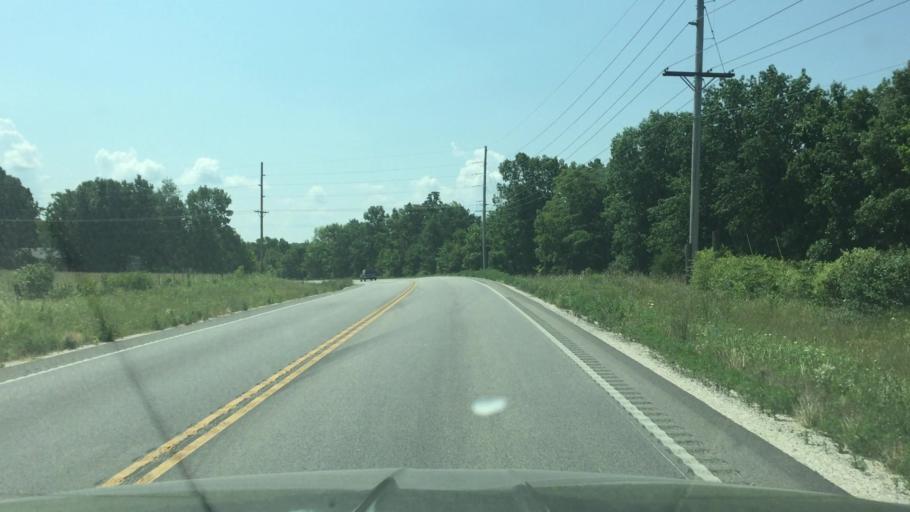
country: US
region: Missouri
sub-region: Miller County
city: Eldon
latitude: 38.3670
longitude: -92.6153
